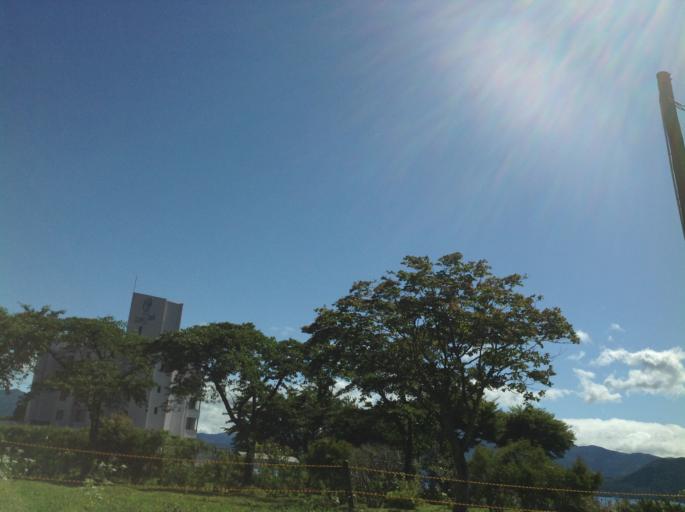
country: JP
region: Akita
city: Kakunodatemachi
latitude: 39.7120
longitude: 140.6339
